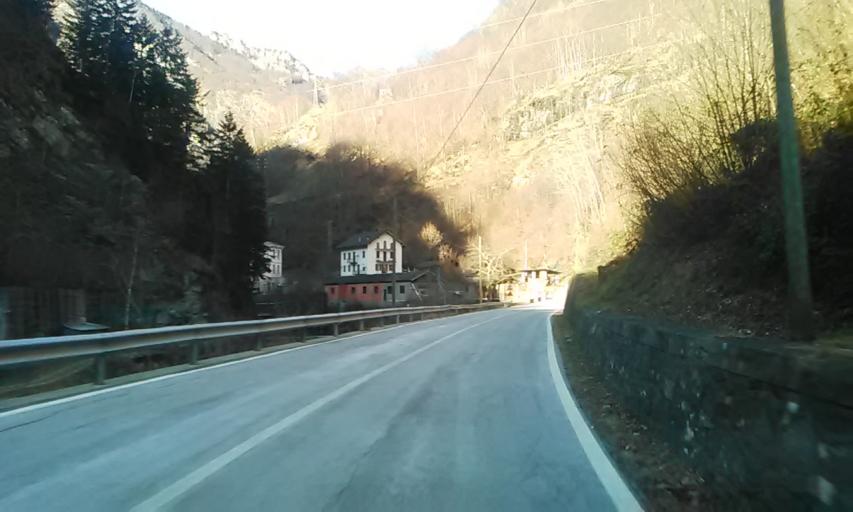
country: IT
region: Piedmont
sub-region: Provincia di Vercelli
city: Rimasco
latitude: 45.8415
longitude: 8.0784
